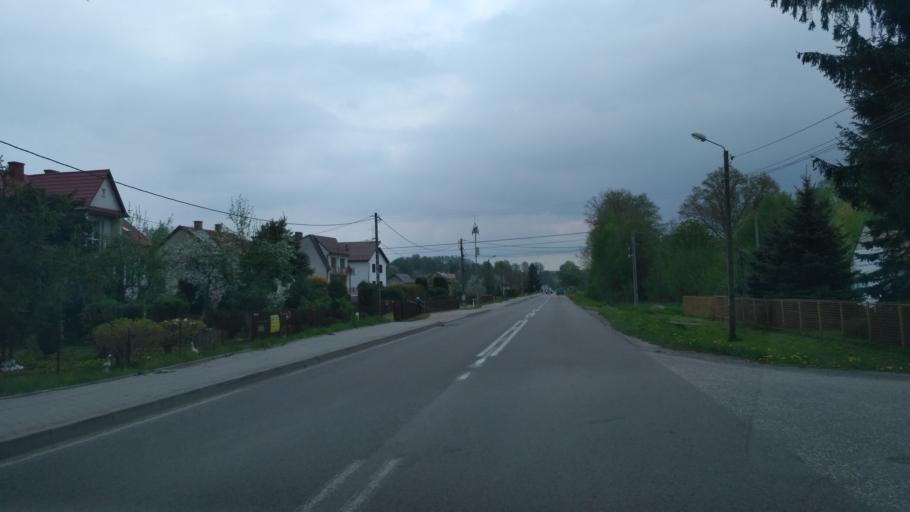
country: PL
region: Lesser Poland Voivodeship
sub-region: Powiat tarnowski
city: Skrzyszow
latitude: 49.9909
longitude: 21.0734
